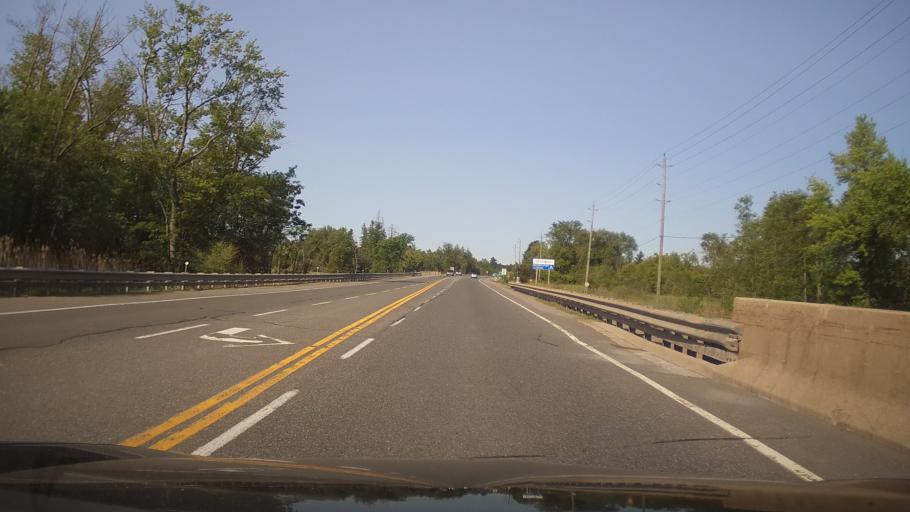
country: CA
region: Ontario
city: Peterborough
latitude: 44.3247
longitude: -78.1575
